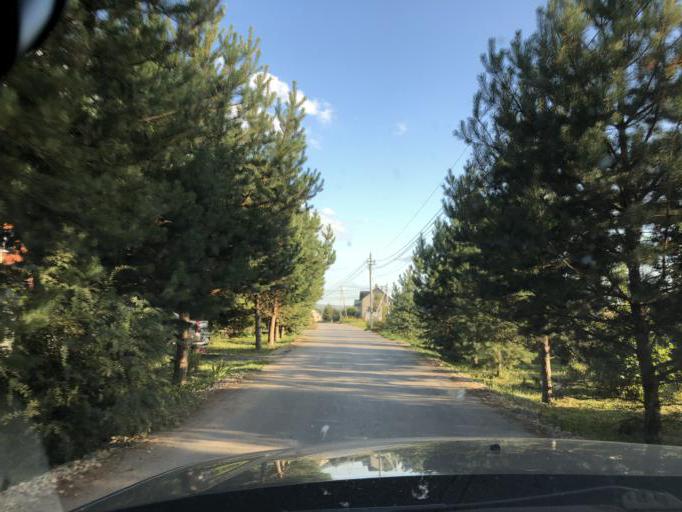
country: RU
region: Tula
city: Kosaya Gora
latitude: 54.1769
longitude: 37.5439
